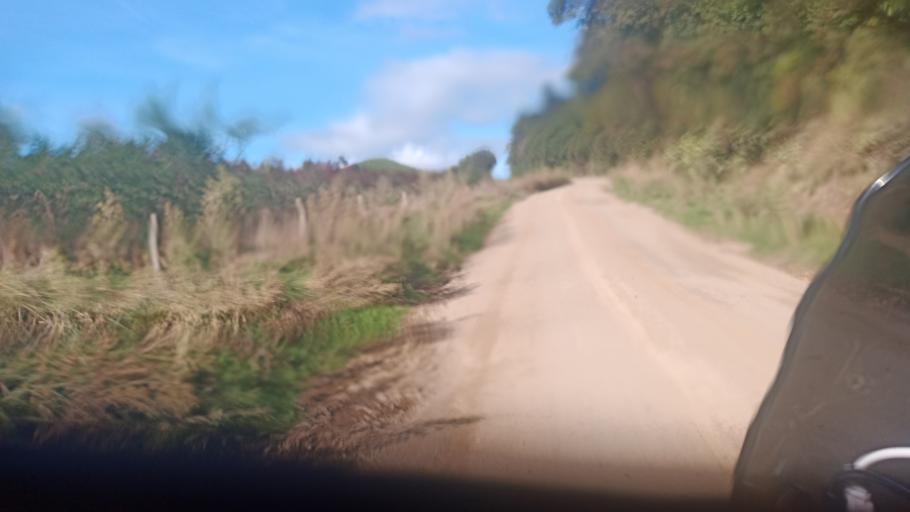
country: NZ
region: Bay of Plenty
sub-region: Opotiki District
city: Opotiki
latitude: -38.4232
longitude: 177.5589
